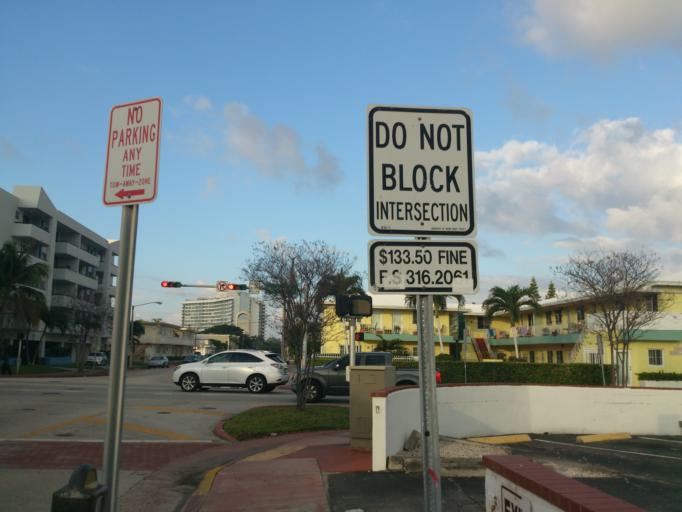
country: US
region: Florida
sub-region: Miami-Dade County
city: Surfside
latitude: 25.8608
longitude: -80.1219
